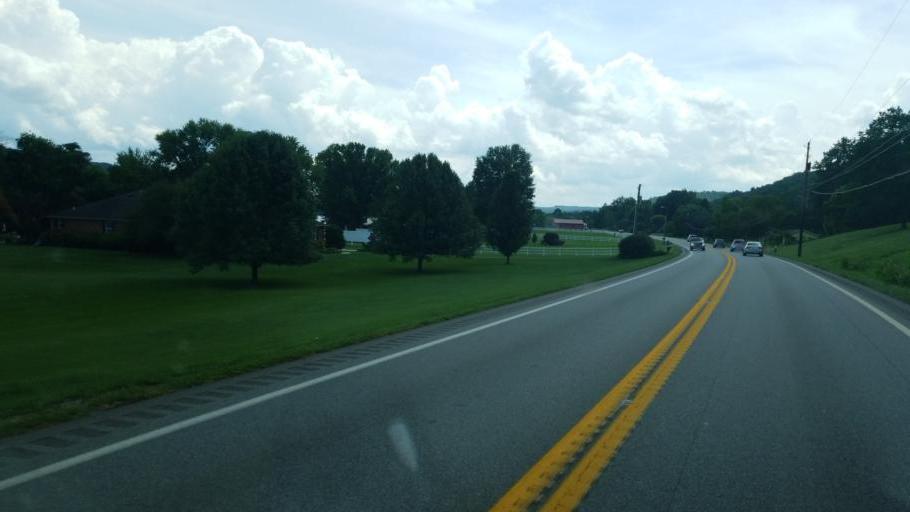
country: US
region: West Virginia
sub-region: Putnam County
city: Buffalo
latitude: 38.5964
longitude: -82.0064
